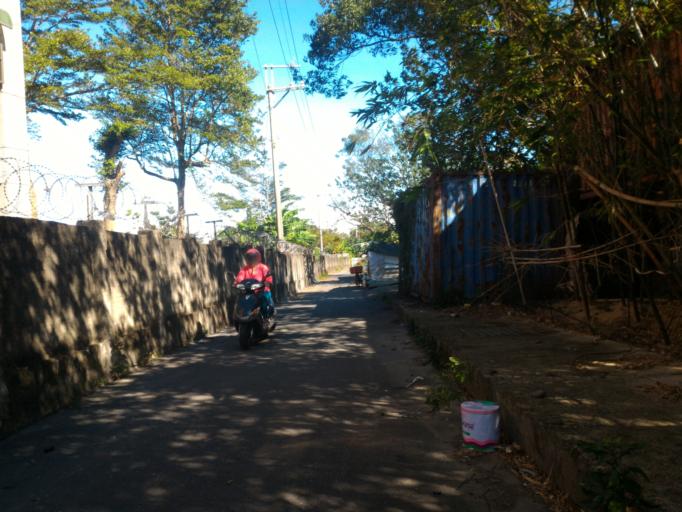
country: TW
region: Taiwan
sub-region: Taoyuan
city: Taoyuan
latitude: 24.9434
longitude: 121.3842
